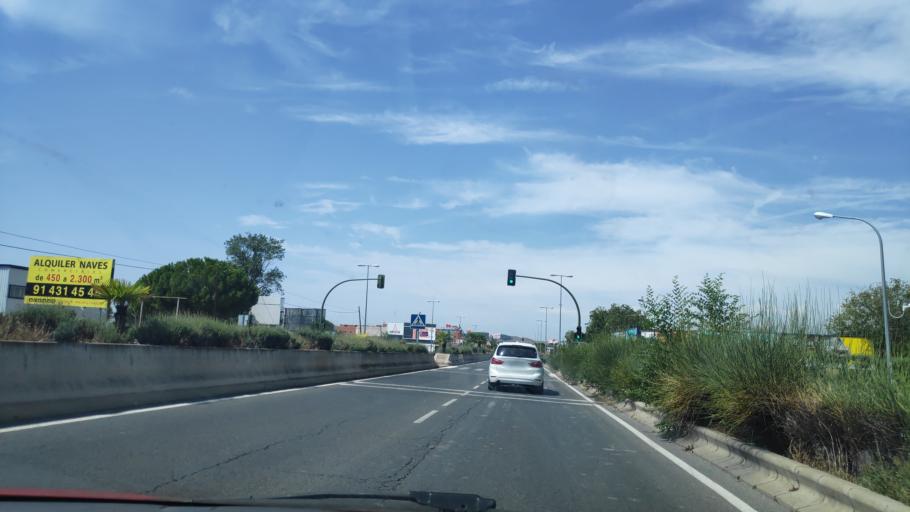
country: ES
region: Madrid
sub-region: Provincia de Madrid
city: Vaciamadrid
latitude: 40.3093
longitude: -3.4769
